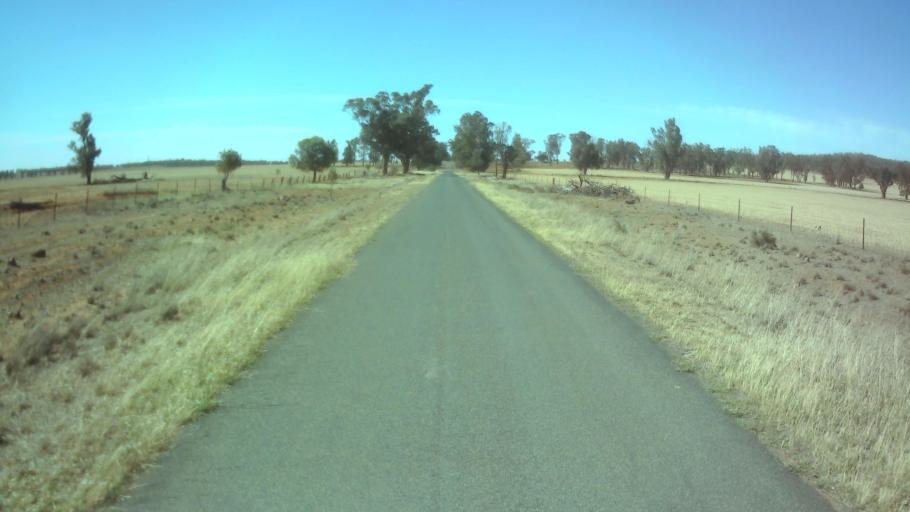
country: AU
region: New South Wales
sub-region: Forbes
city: Forbes
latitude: -33.7362
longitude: 147.7418
